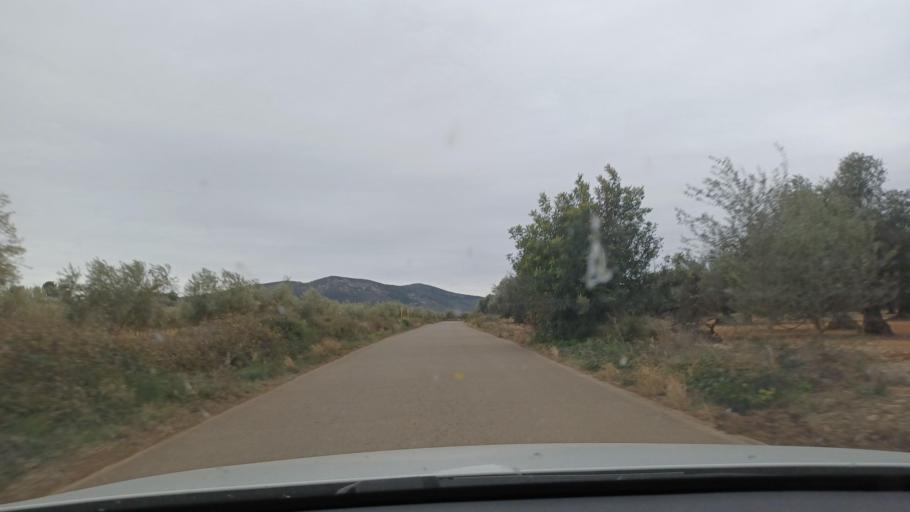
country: ES
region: Valencia
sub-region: Provincia de Castello
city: Canet lo Roig
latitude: 40.5695
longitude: 0.2757
